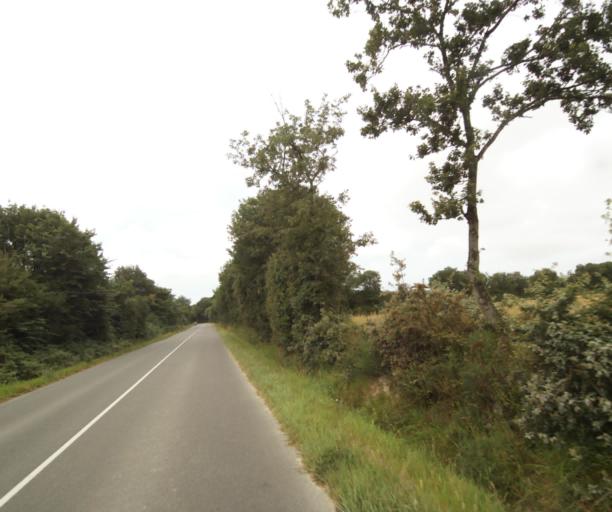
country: FR
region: Pays de la Loire
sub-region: Departement de la Vendee
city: Chateau-d'Olonne
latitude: 46.4939
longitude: -1.7015
